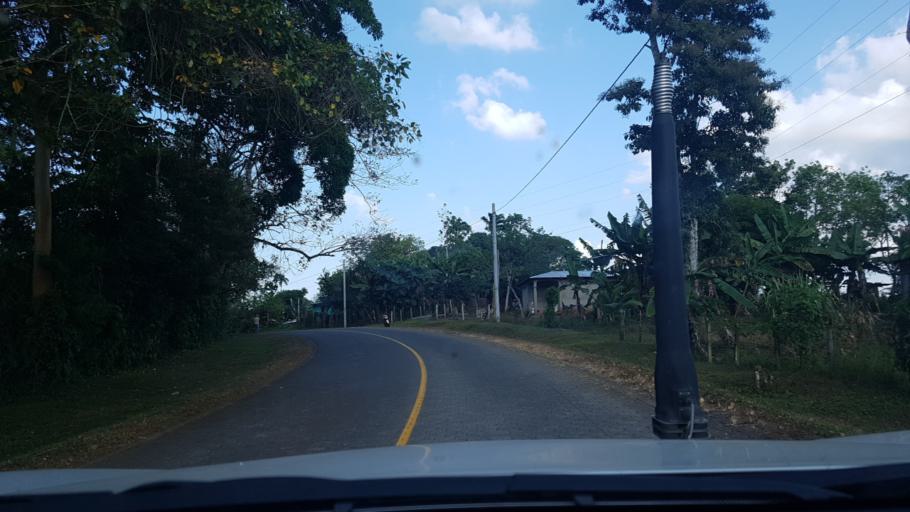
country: NI
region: Atlantico Sur
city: Nueva Guinea
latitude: 11.6943
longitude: -84.3993
